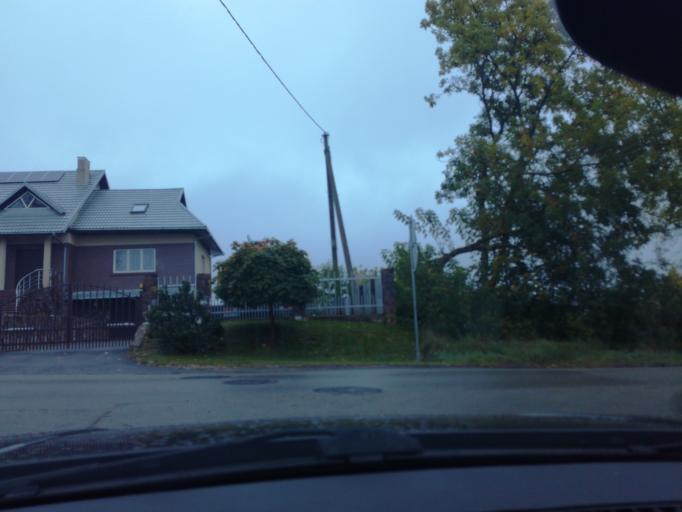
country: LT
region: Alytaus apskritis
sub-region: Alytus
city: Alytus
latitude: 54.3978
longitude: 24.1006
